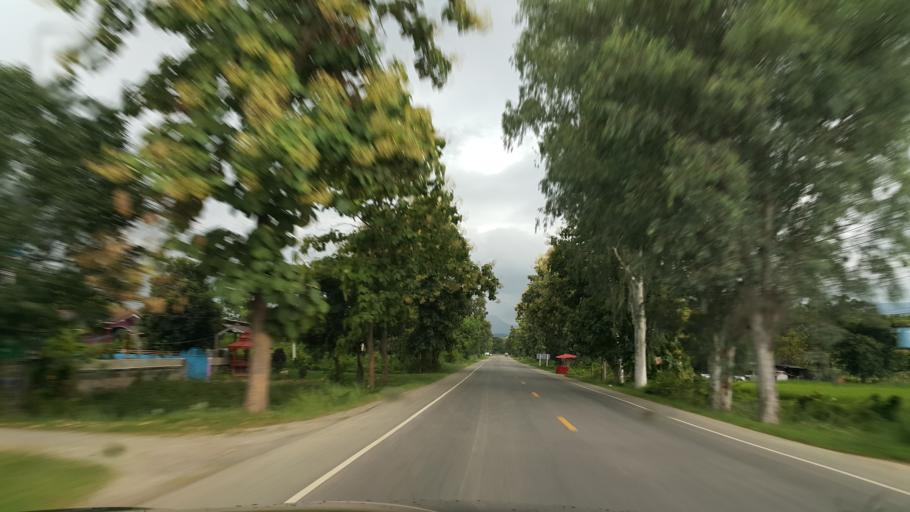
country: TH
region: Phayao
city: Dok Kham Tai
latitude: 19.2255
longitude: 100.0458
